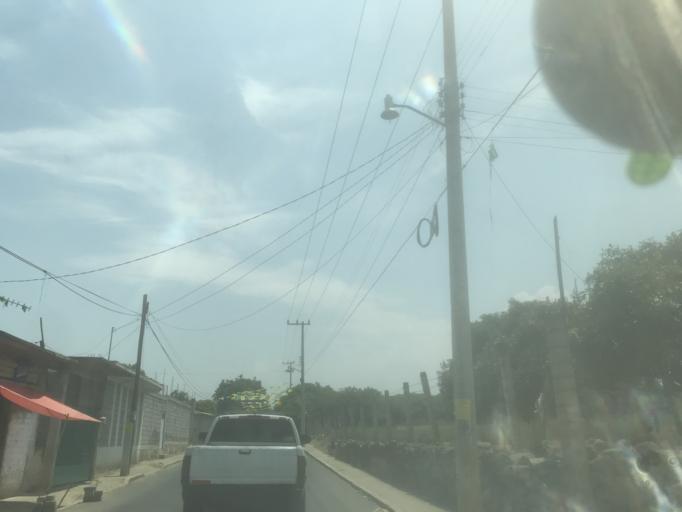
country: MX
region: Mexico
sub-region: Ozumba
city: San Jose Tlacotitlan
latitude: 18.9861
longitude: -98.8069
